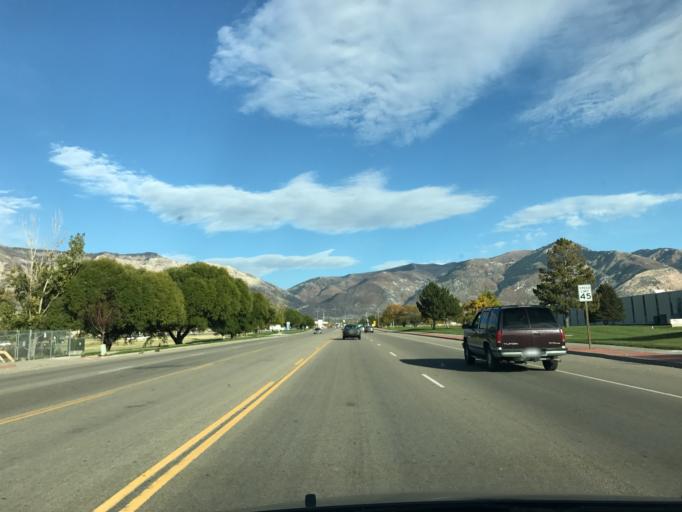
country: US
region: Utah
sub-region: Weber County
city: Farr West
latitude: 41.3068
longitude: -112.0149
